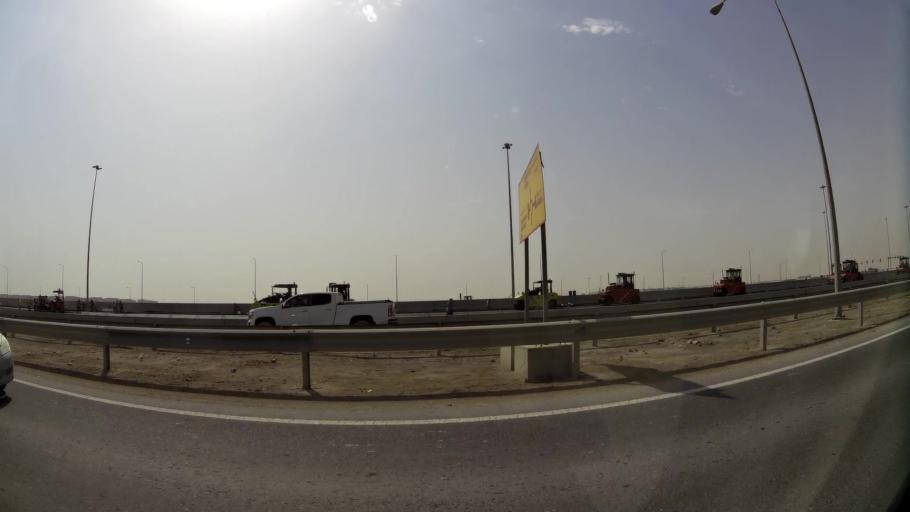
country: QA
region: Al Wakrah
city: Al Wukayr
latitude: 25.2025
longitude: 51.4773
